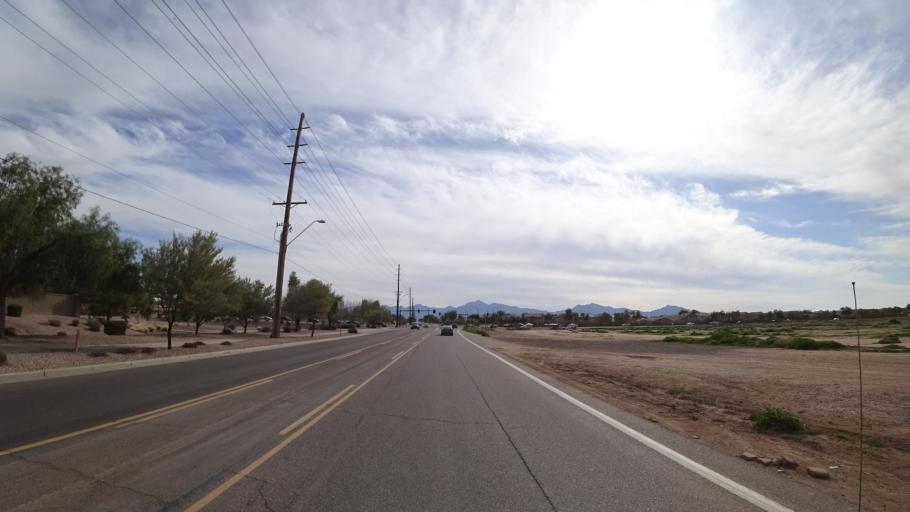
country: US
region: Arizona
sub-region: Maricopa County
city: Tolleson
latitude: 33.4227
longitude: -112.2556
